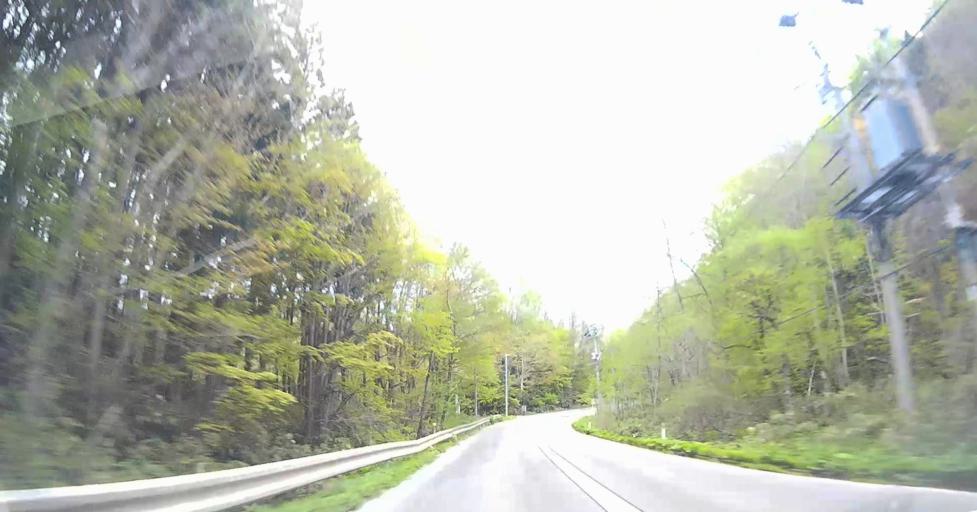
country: JP
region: Aomori
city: Goshogawara
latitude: 41.1129
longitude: 140.5326
